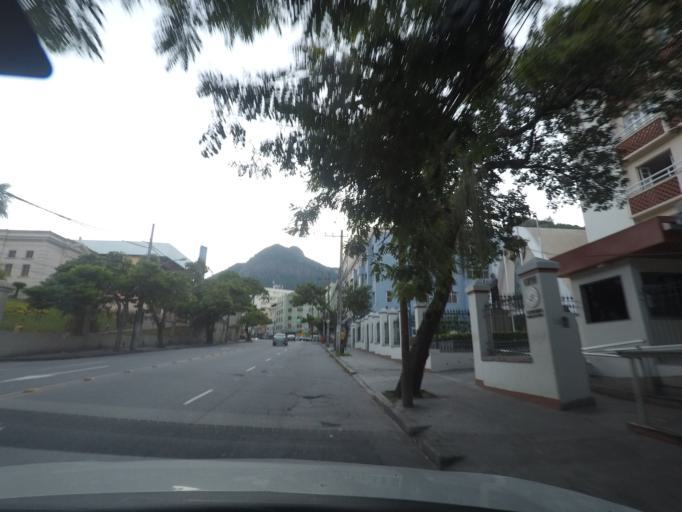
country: BR
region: Rio de Janeiro
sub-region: Rio De Janeiro
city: Rio de Janeiro
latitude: -22.9409
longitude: -43.2511
